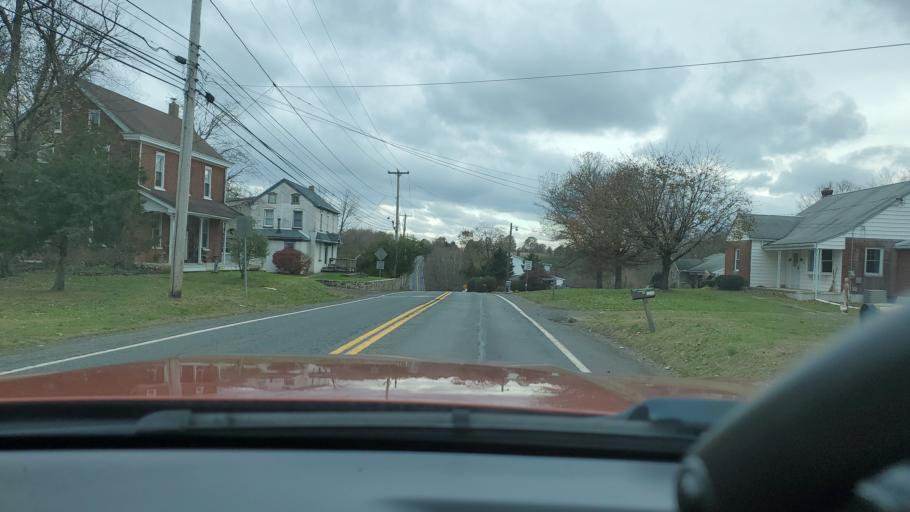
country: US
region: Pennsylvania
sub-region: Montgomery County
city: Spring Mount
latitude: 40.2778
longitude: -75.4841
